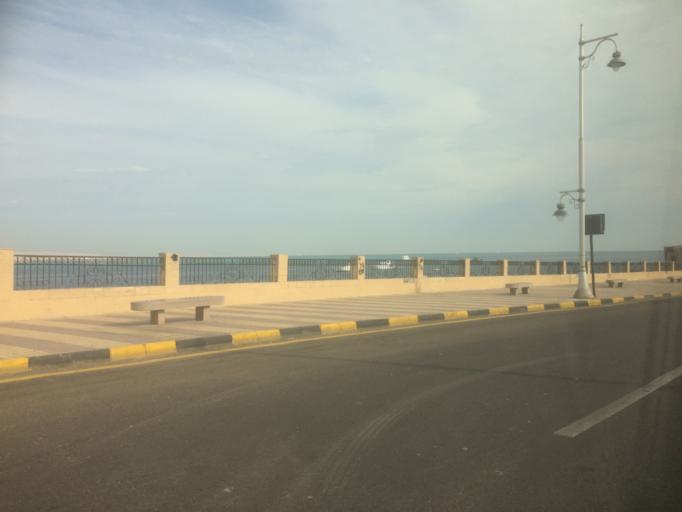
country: EG
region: Red Sea
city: Hurghada
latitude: 27.2036
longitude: 33.8496
